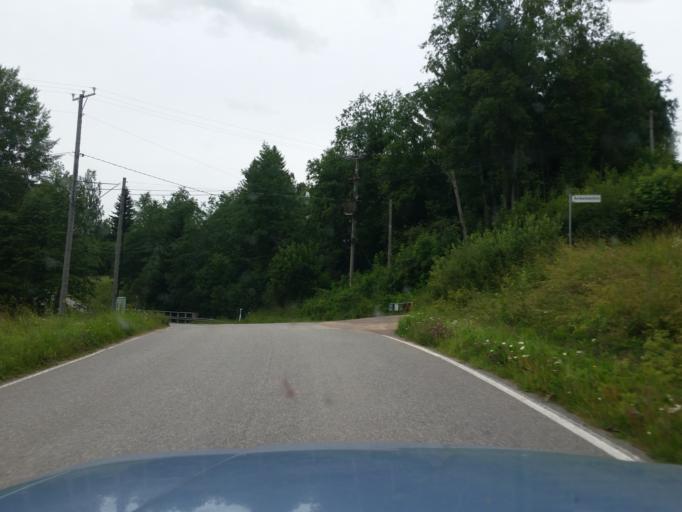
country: FI
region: Uusimaa
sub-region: Helsinki
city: Sammatti
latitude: 60.4703
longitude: 23.8412
